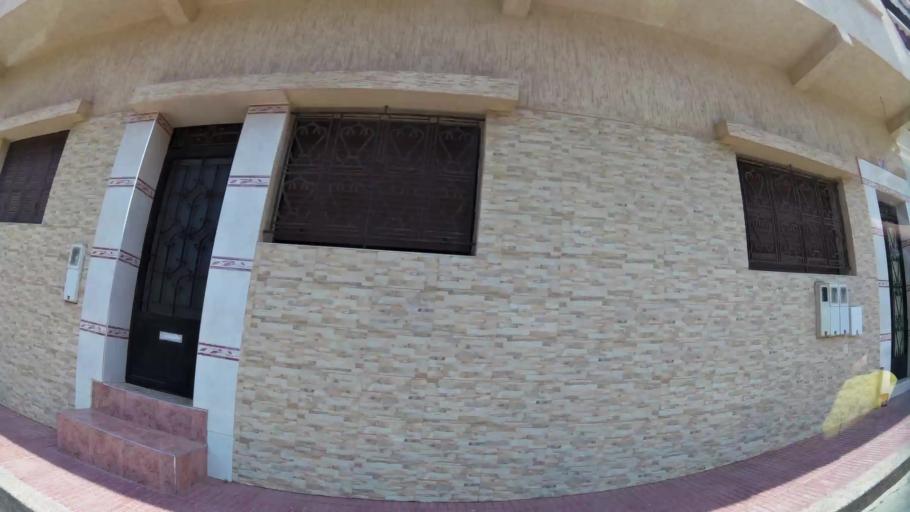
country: MA
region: Rabat-Sale-Zemmour-Zaer
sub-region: Skhirate-Temara
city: Temara
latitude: 33.9793
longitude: -6.8922
